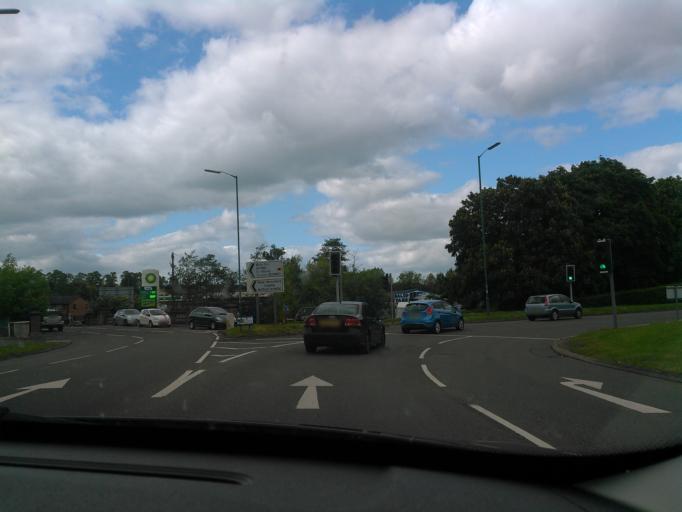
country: GB
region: England
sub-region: Shropshire
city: Bayston Hill
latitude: 52.6912
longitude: -2.7551
